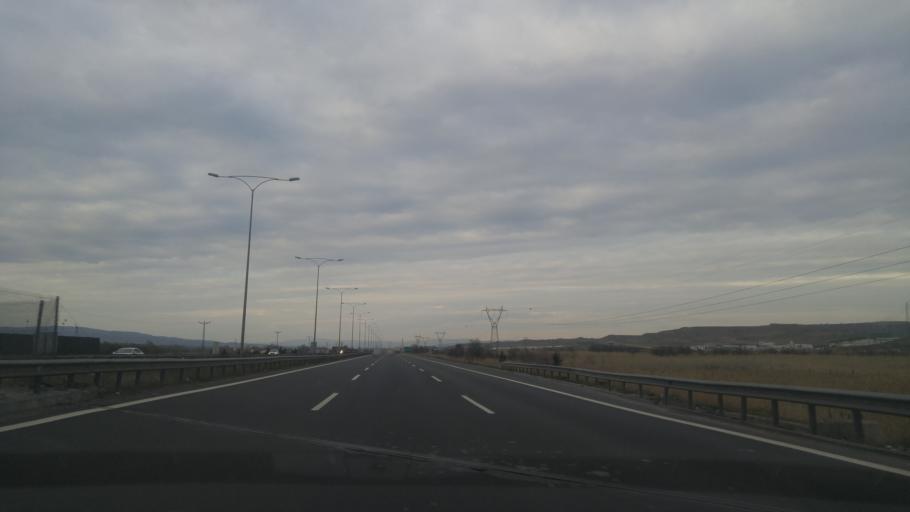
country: TR
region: Ankara
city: Etimesgut
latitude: 40.0851
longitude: 32.6083
